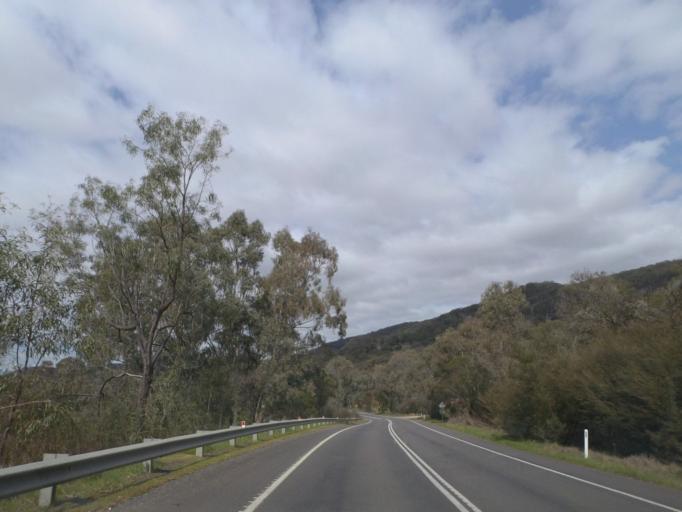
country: AU
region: Victoria
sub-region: Murrindindi
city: Kinglake West
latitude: -37.1245
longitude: 145.2214
